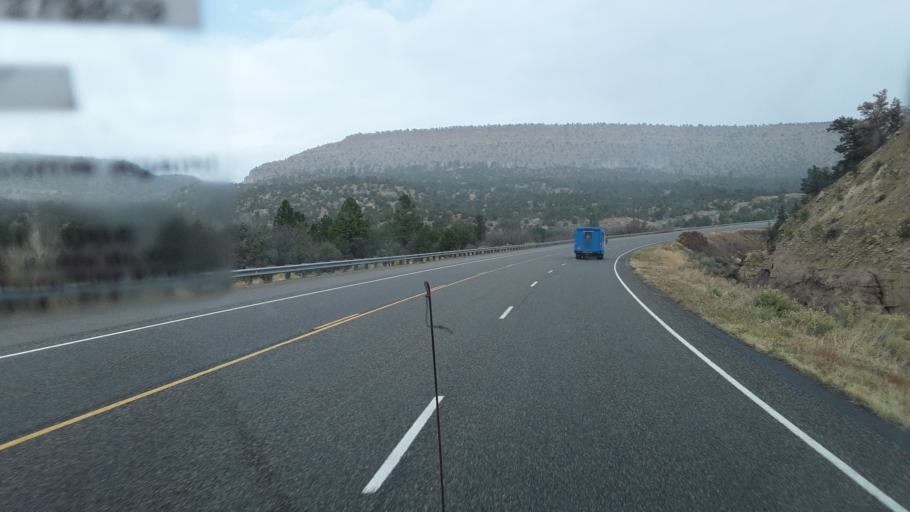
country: US
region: New Mexico
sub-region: Rio Arriba County
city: Santa Teresa
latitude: 36.3978
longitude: -106.4942
